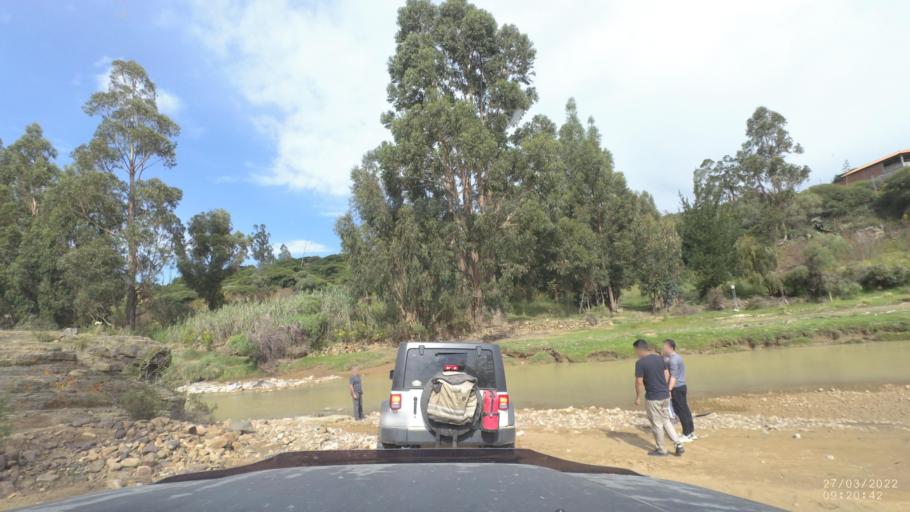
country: BO
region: Cochabamba
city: Cliza
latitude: -17.7306
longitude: -65.8749
